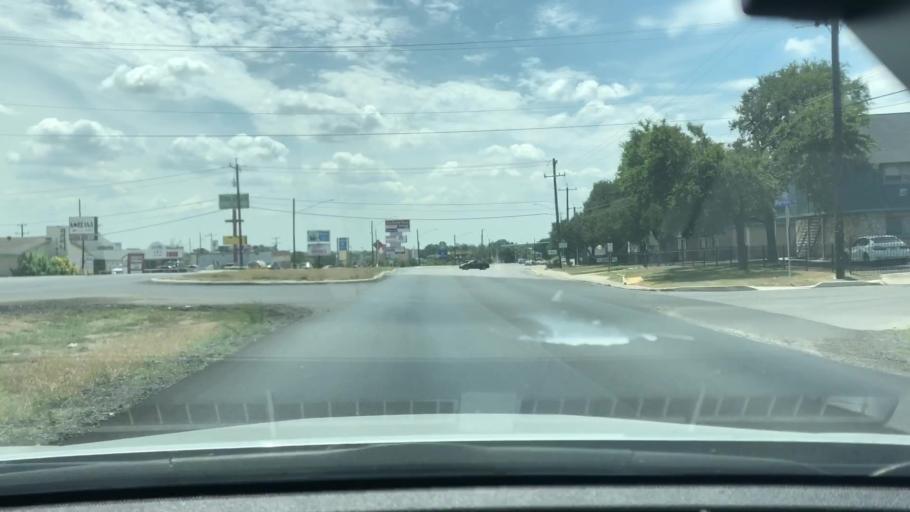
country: US
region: Texas
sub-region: Bexar County
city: Terrell Hills
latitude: 29.4875
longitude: -98.4302
